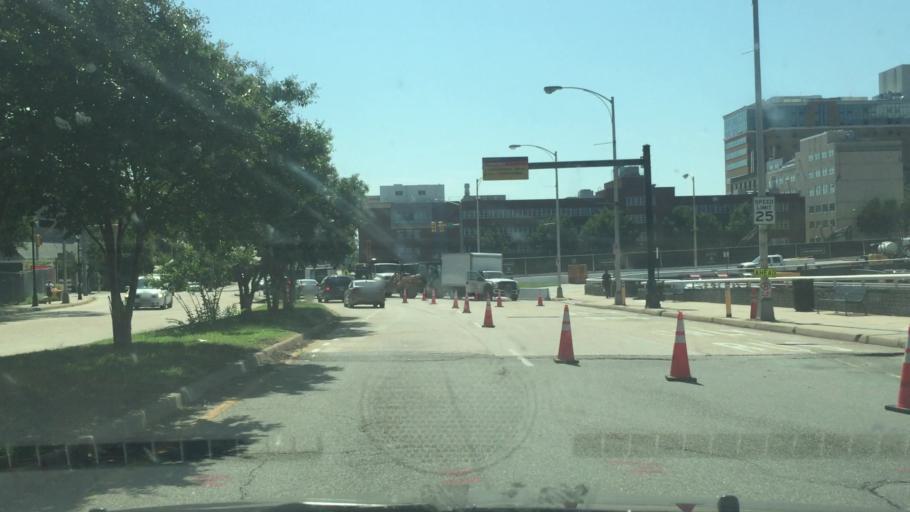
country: US
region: Virginia
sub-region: City of Richmond
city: Richmond
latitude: 37.5435
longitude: -77.4312
